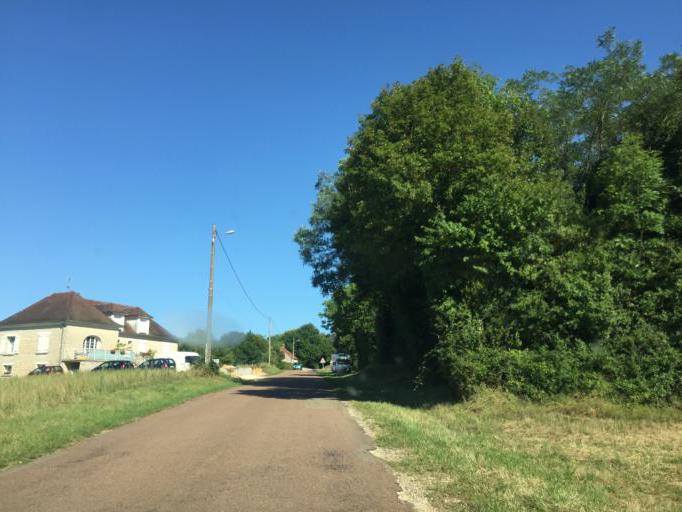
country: FR
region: Bourgogne
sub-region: Departement de l'Yonne
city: Fontenailles
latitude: 47.5033
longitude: 3.3526
